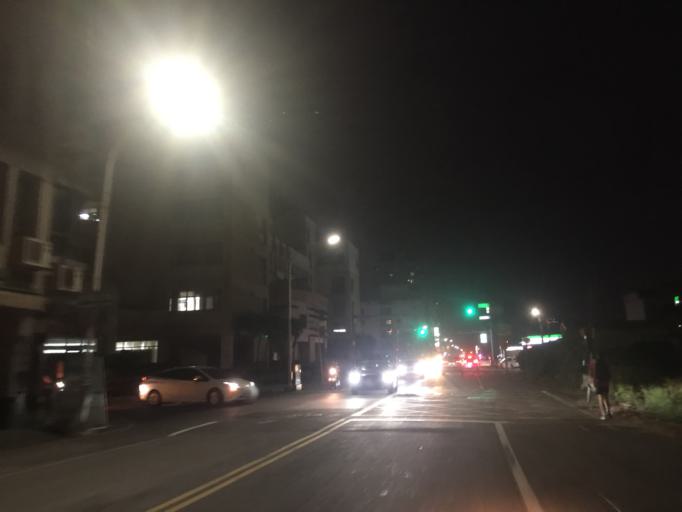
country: TW
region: Taiwan
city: Xinying
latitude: 23.3148
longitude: 120.3231
